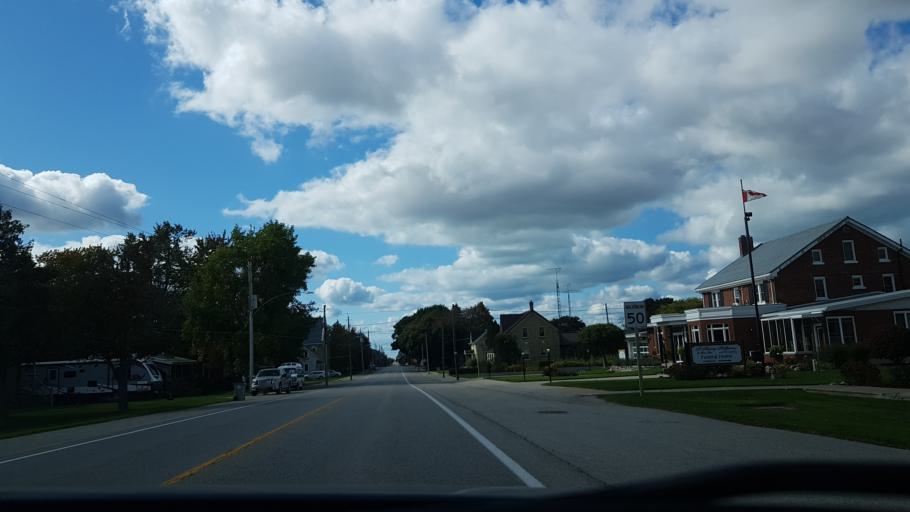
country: CA
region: Ontario
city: South Huron
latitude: 43.3467
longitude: -81.6296
